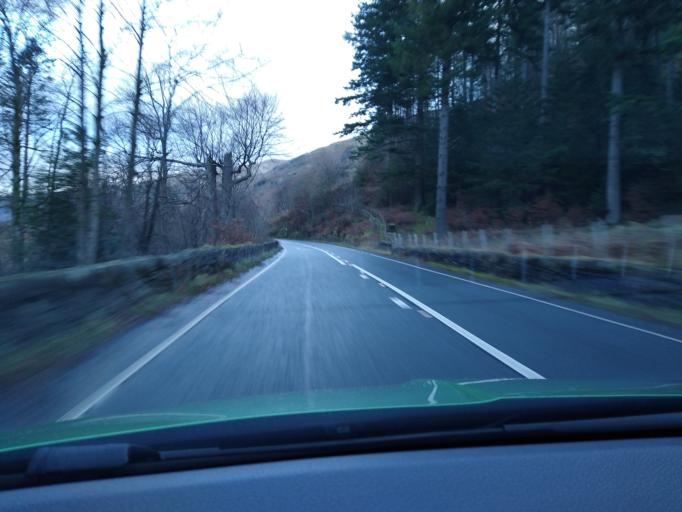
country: GB
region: England
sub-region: Cumbria
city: Keswick
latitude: 54.5408
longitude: -3.0597
